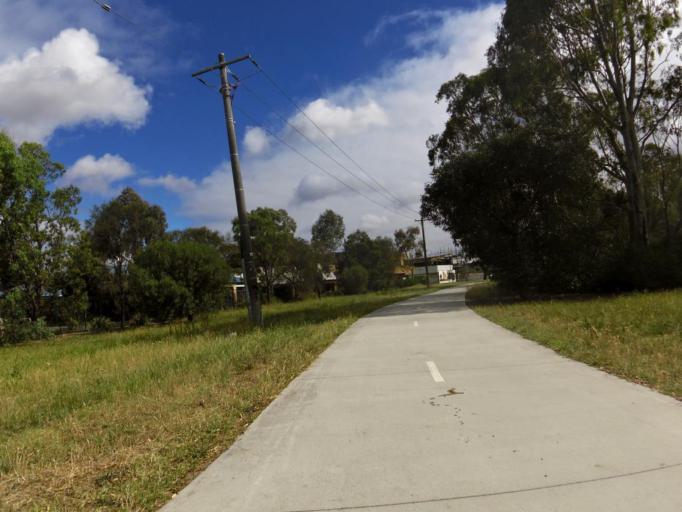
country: AU
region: Victoria
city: Heidelberg West
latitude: -37.7623
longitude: 145.0274
